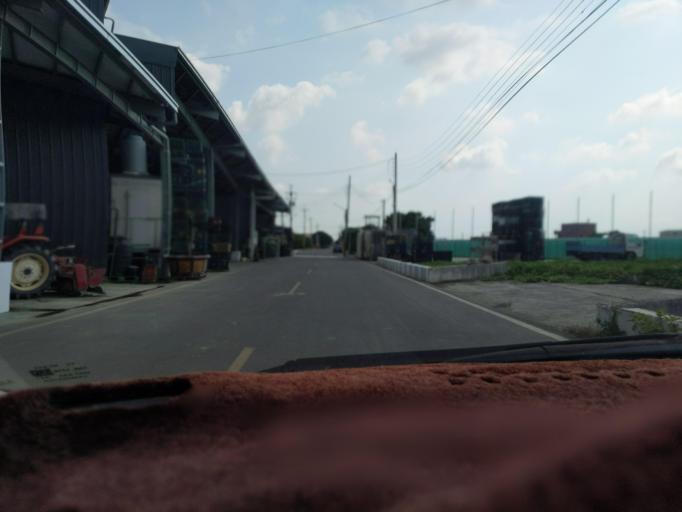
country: TW
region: Taiwan
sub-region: Yunlin
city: Douliu
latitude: 23.7930
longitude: 120.4194
